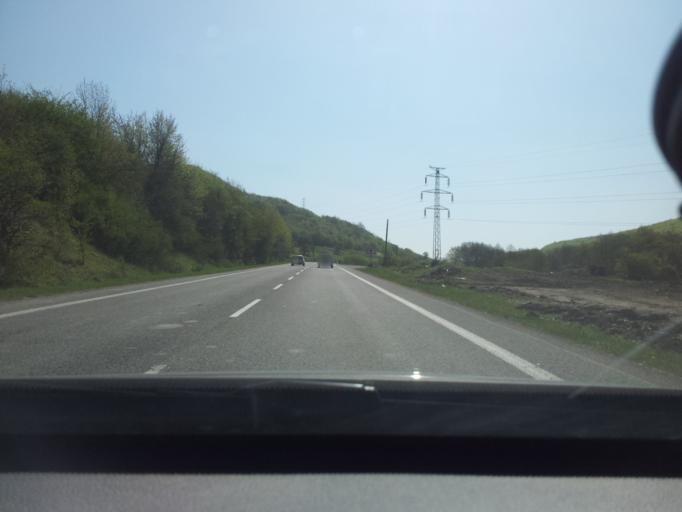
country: SK
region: Trenciansky
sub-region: Okres Trencin
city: Trencin
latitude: 48.8246
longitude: 18.0699
